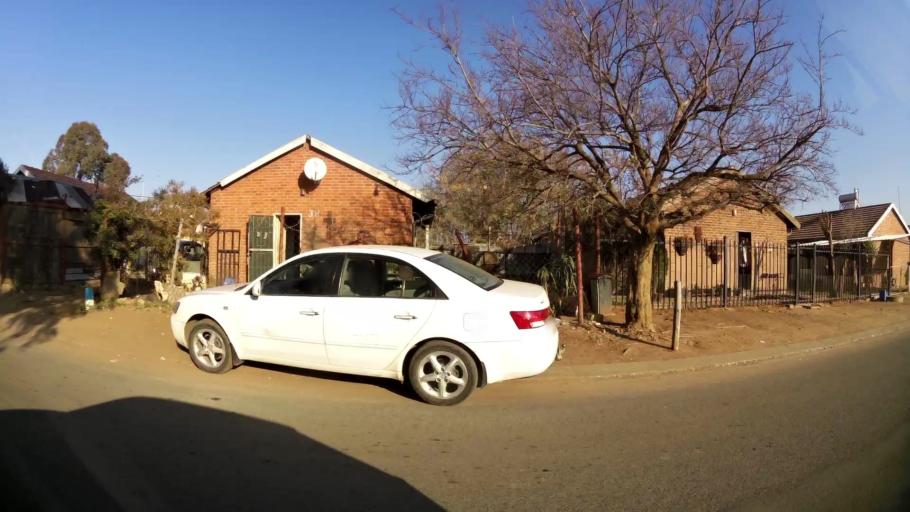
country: ZA
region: Orange Free State
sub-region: Mangaung Metropolitan Municipality
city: Bloemfontein
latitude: -29.1565
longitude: 26.2160
